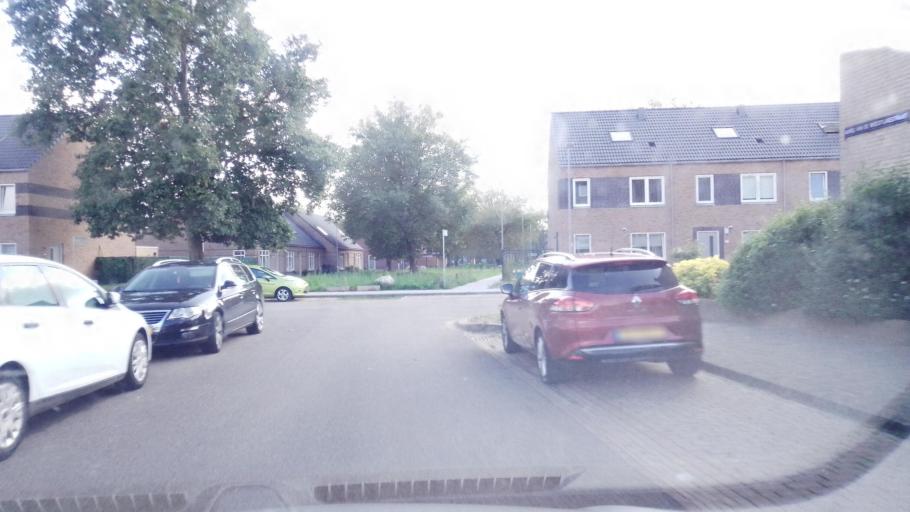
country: NL
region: Limburg
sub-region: Gemeente Venlo
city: Tegelen
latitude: 51.3720
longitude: 6.1389
